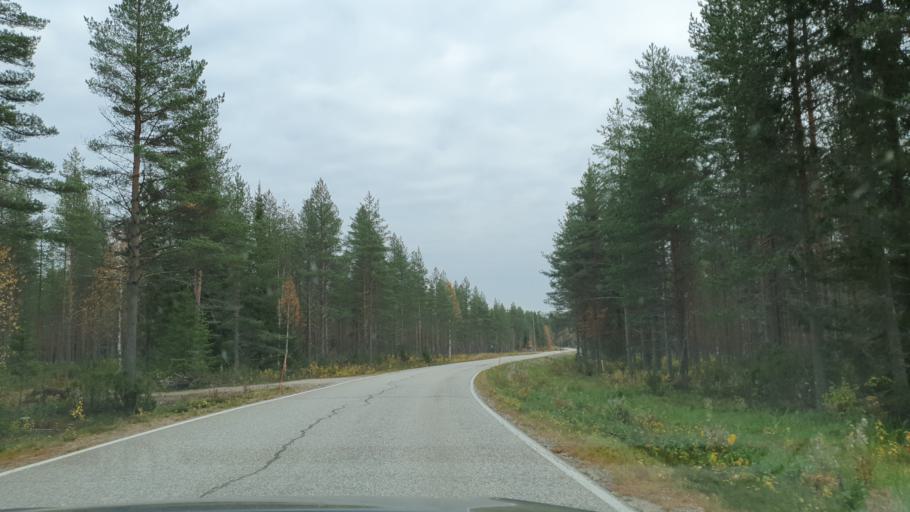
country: FI
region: Kainuu
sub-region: Kajaani
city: Ristijaervi
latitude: 64.4627
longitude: 28.3148
